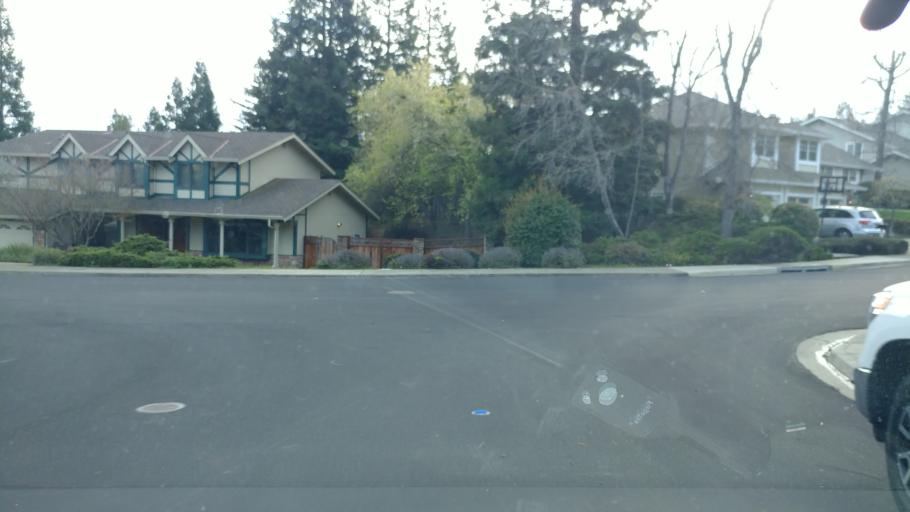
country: US
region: California
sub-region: Contra Costa County
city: Diablo
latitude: 37.8225
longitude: -121.9759
